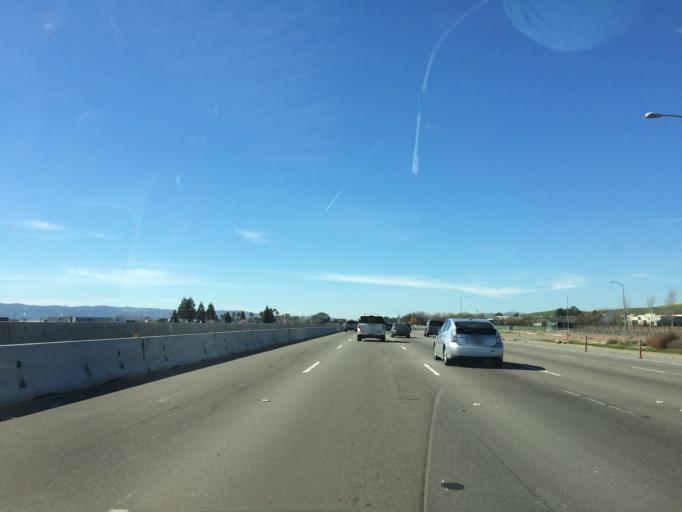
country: US
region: California
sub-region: Alameda County
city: Livermore
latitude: 37.7010
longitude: -121.8038
